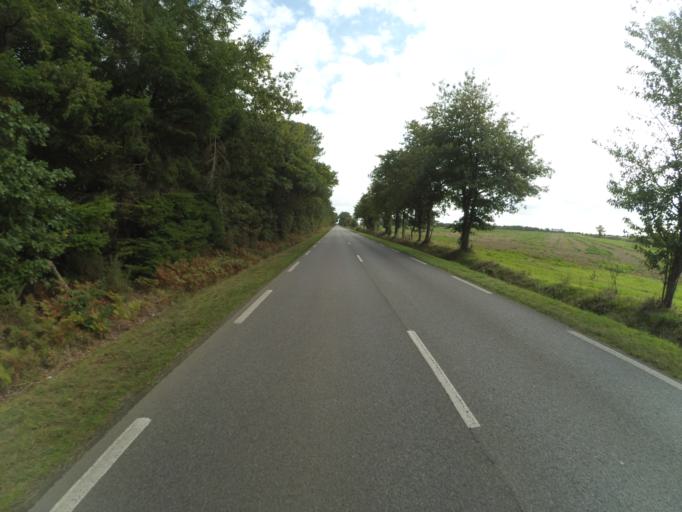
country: FR
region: Pays de la Loire
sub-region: Departement de la Loire-Atlantique
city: Plesse
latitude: 47.4947
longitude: -1.8624
